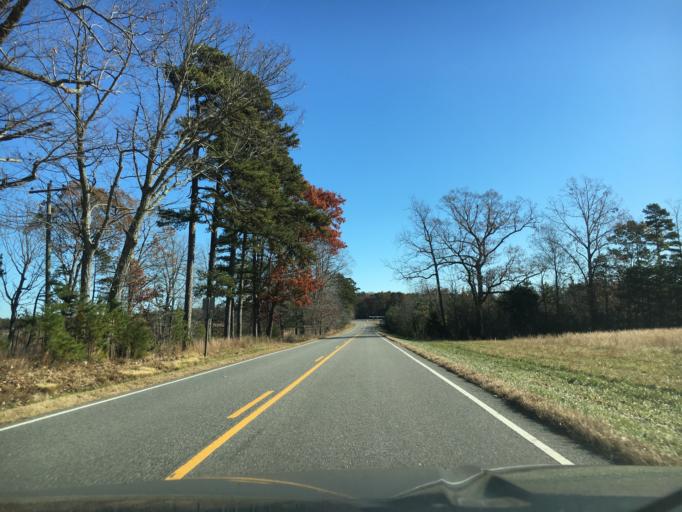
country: US
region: Virginia
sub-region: Buckingham County
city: Buckingham
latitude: 37.4575
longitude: -78.6841
